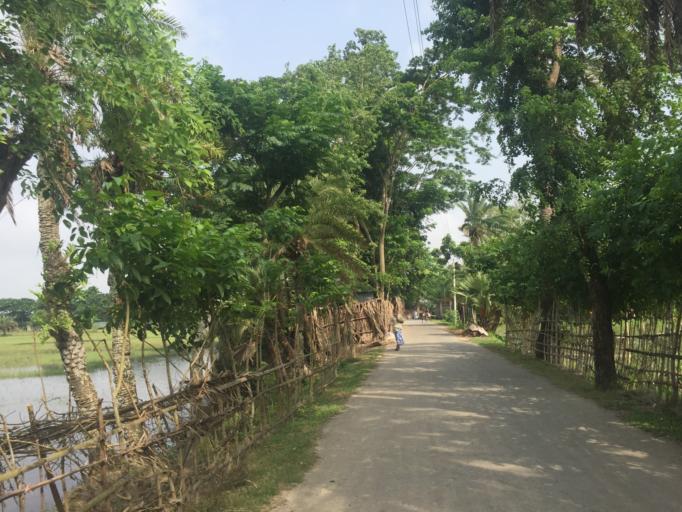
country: BD
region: Barisal
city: Mathba
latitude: 22.2134
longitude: 89.9213
